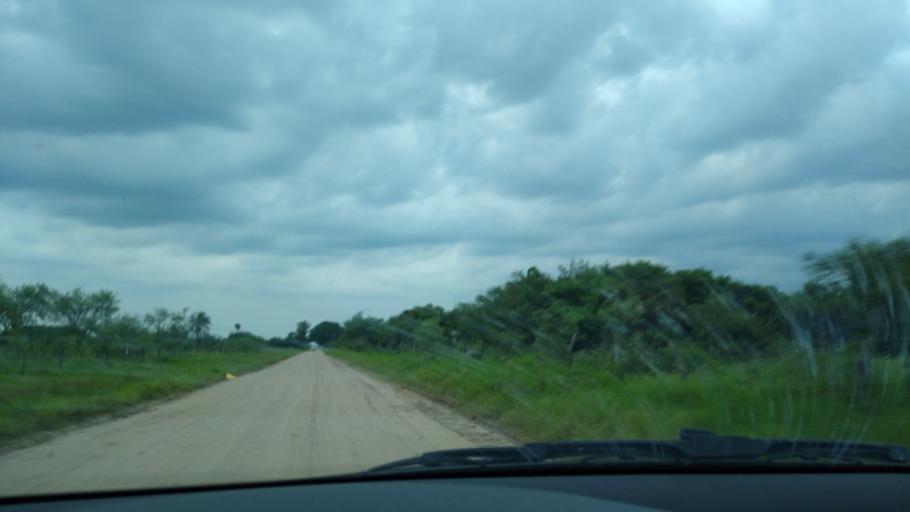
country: AR
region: Chaco
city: Puerto Vilelas
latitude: -27.5101
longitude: -58.9666
